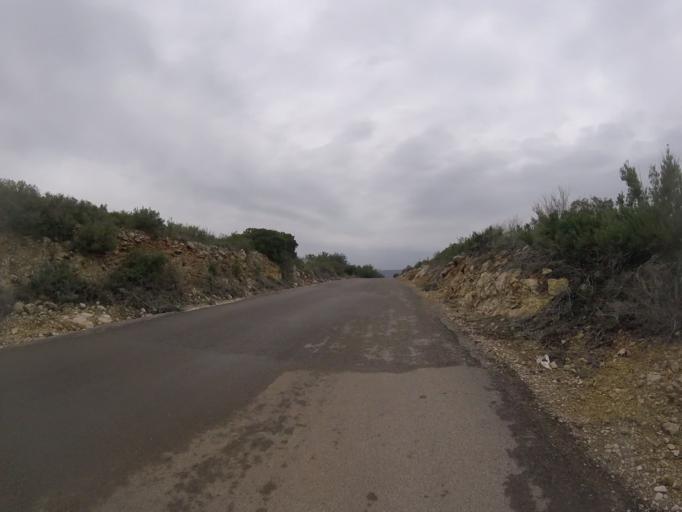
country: ES
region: Valencia
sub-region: Provincia de Castello
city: Alcala de Xivert
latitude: 40.2813
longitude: 0.2289
